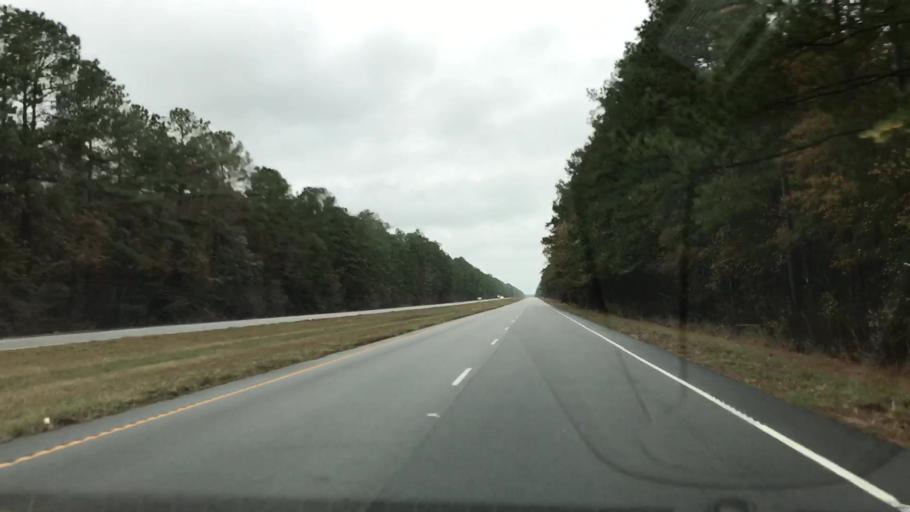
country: US
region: South Carolina
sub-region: Charleston County
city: Awendaw
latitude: 33.1468
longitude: -79.4355
